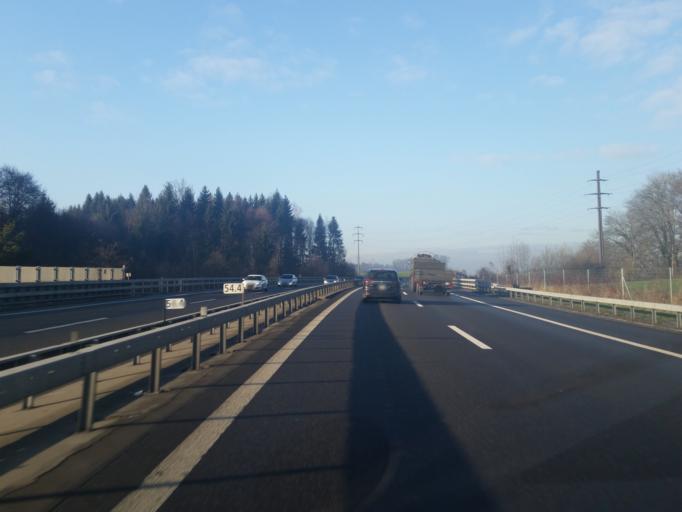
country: CH
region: Zurich
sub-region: Bezirk Affoltern
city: Knonau
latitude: 47.2300
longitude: 8.4602
